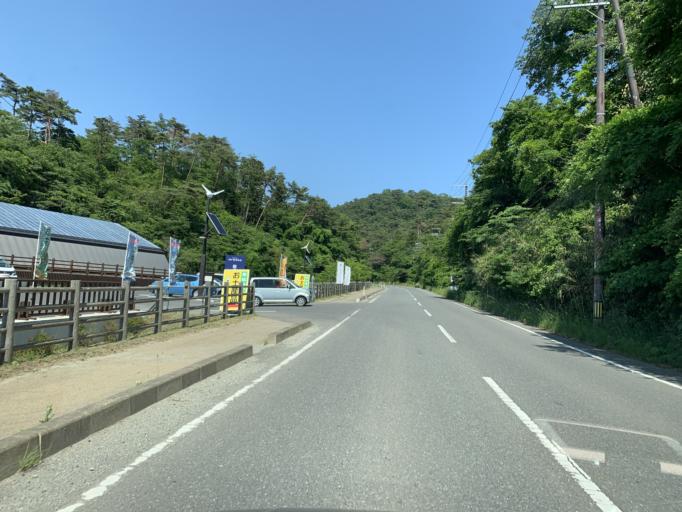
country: JP
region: Miyagi
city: Matsushima
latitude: 38.3428
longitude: 141.1504
